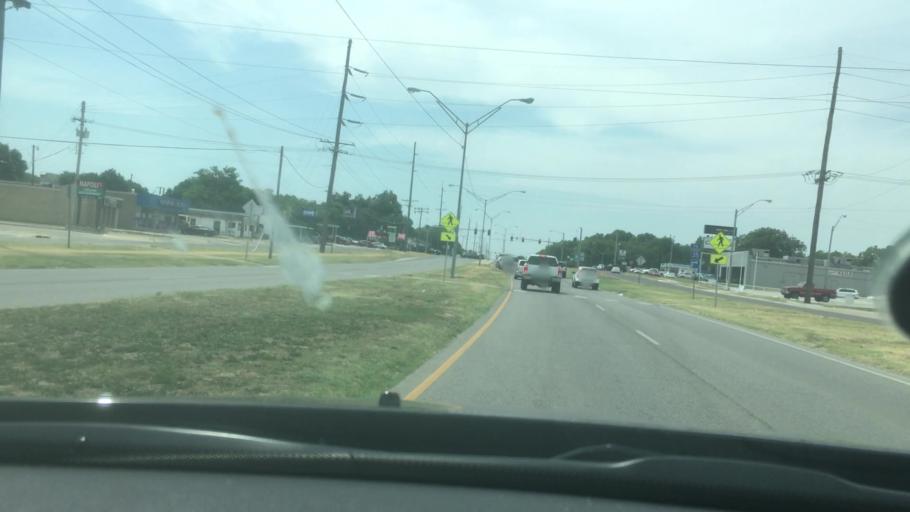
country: US
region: Oklahoma
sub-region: Carter County
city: Ardmore
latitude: 34.1766
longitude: -97.1434
